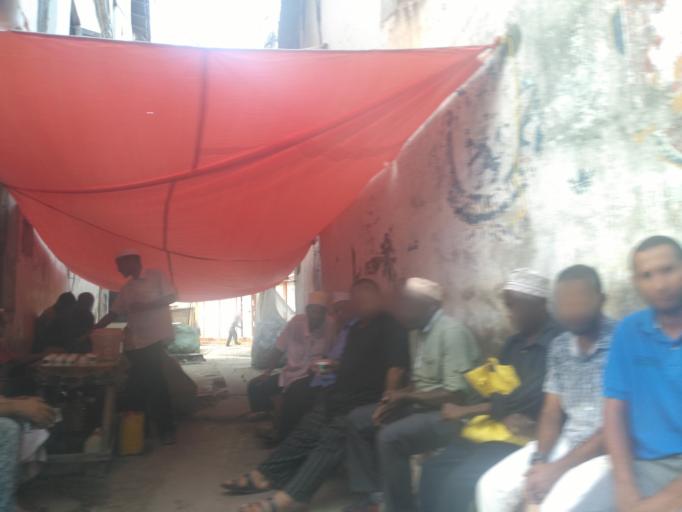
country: TZ
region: Zanzibar Urban/West
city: Zanzibar
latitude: -6.1613
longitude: 39.1959
